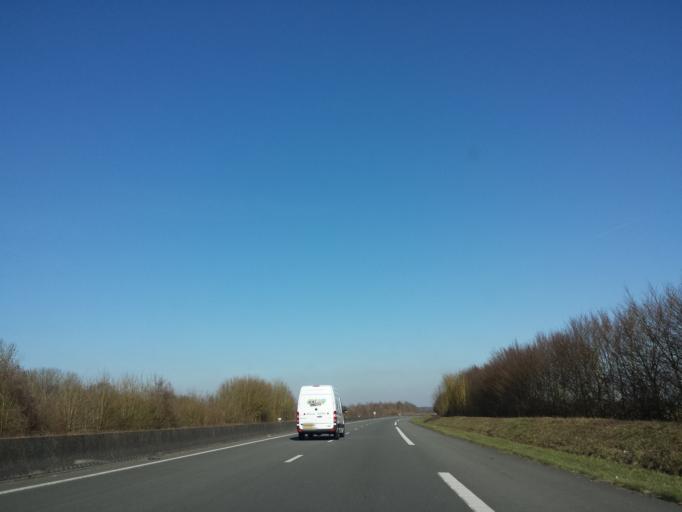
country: FR
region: Picardie
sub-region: Departement de l'Oise
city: Breteuil
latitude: 49.6238
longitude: 2.2087
